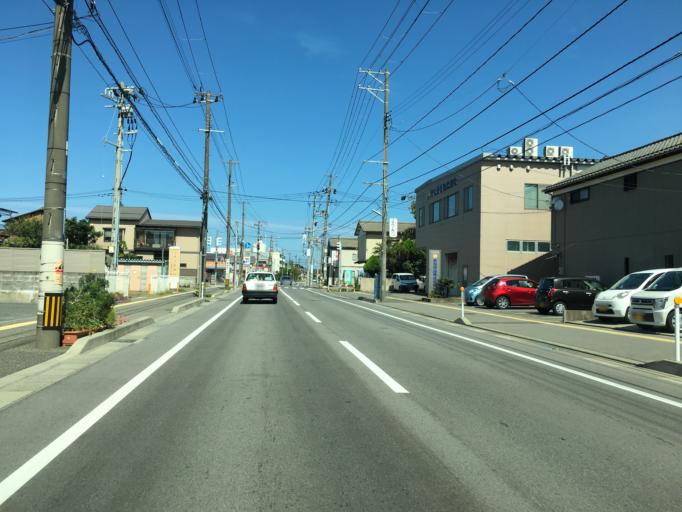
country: JP
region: Niigata
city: Niigata-shi
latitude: 37.9343
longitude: 139.0570
